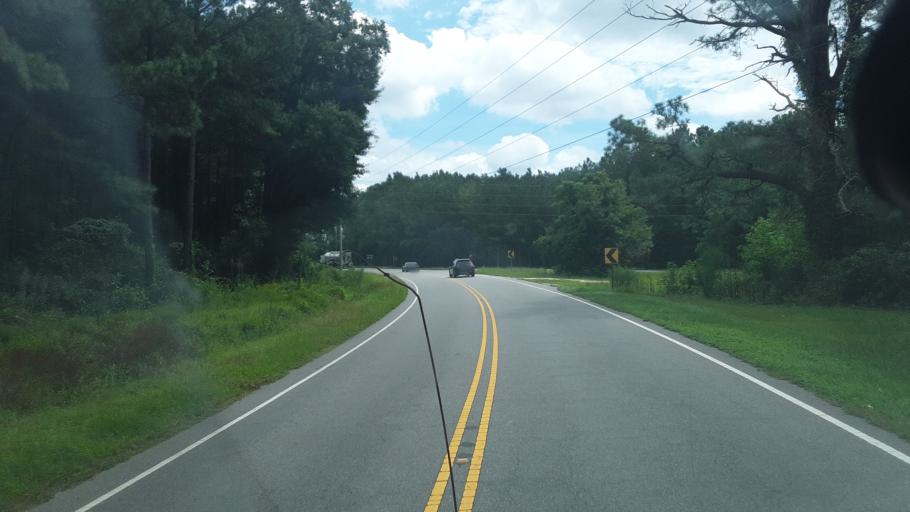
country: US
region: North Carolina
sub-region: Robeson County
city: Rowland
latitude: 34.4761
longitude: -79.2364
